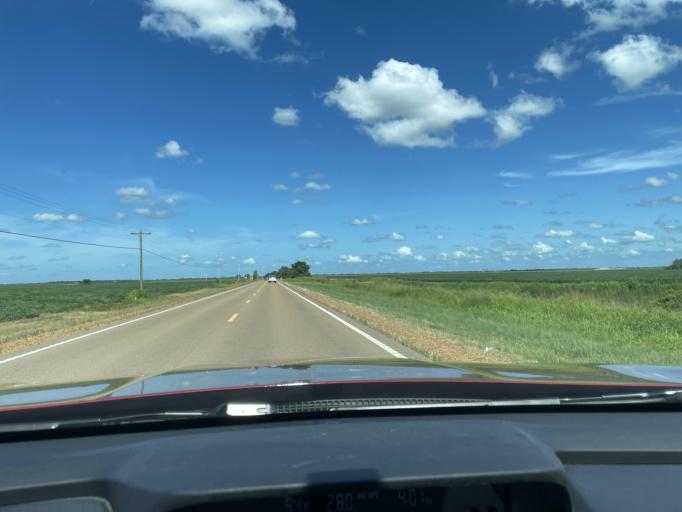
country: US
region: Mississippi
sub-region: Humphreys County
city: Belzoni
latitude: 33.1838
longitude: -90.5455
